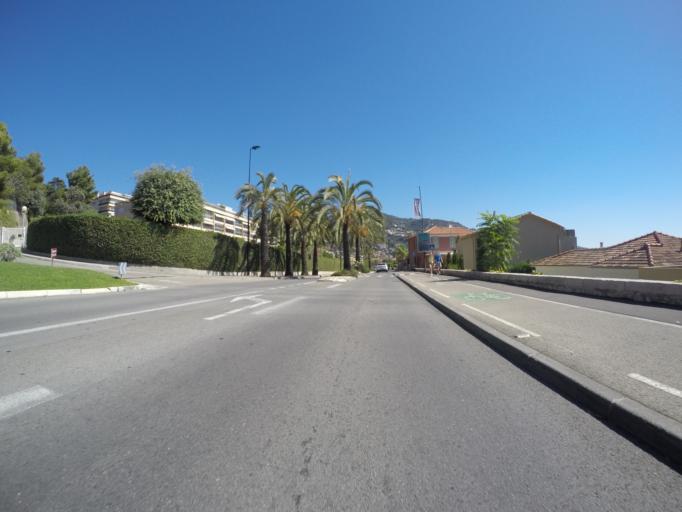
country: FR
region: Provence-Alpes-Cote d'Azur
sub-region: Departement des Alpes-Maritimes
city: Villefranche-sur-Mer
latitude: 43.6980
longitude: 7.3047
